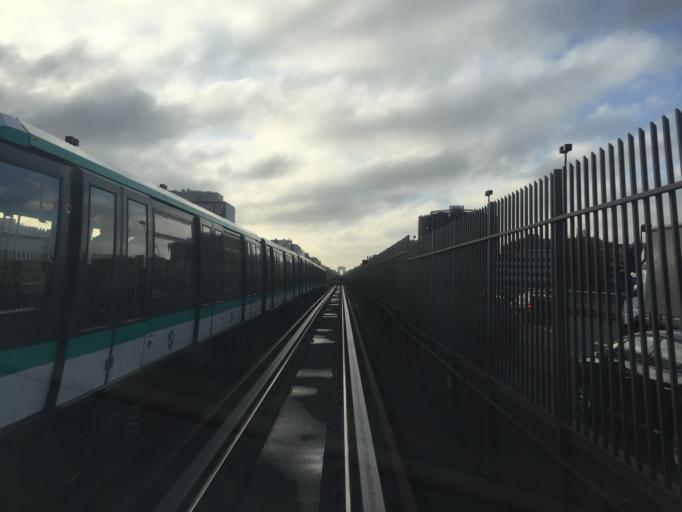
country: FR
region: Ile-de-France
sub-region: Departement des Hauts-de-Seine
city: Courbevoie
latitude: 48.8871
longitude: 2.2532
